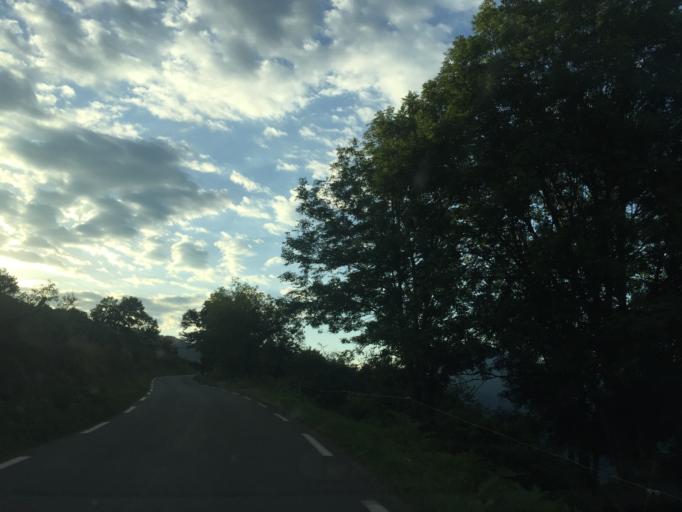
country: FR
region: Midi-Pyrenees
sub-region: Departement des Hautes-Pyrenees
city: Saint-Lary-Soulan
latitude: 42.9255
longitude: 0.3517
